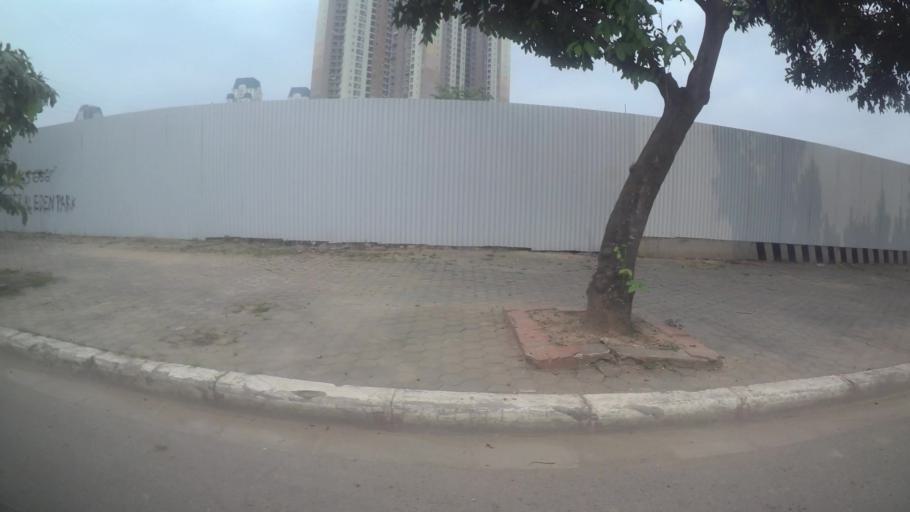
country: VN
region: Ha Noi
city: Cau Dien
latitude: 21.0102
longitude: 105.7731
